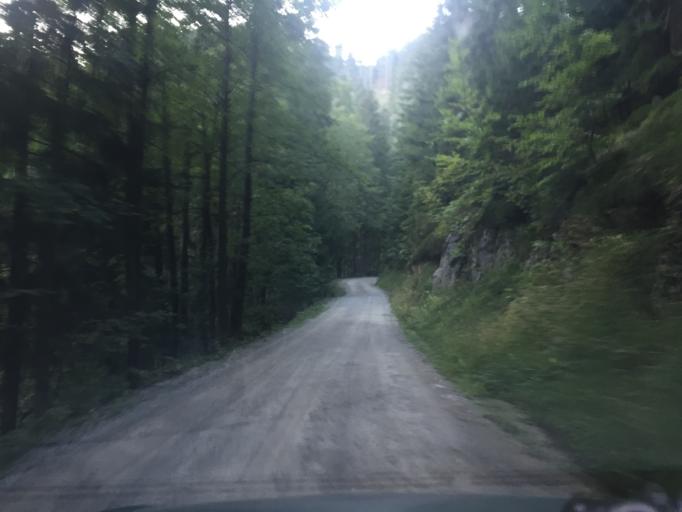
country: SI
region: Ravne na Koroskem
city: Kotlje
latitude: 46.4575
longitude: 14.9752
